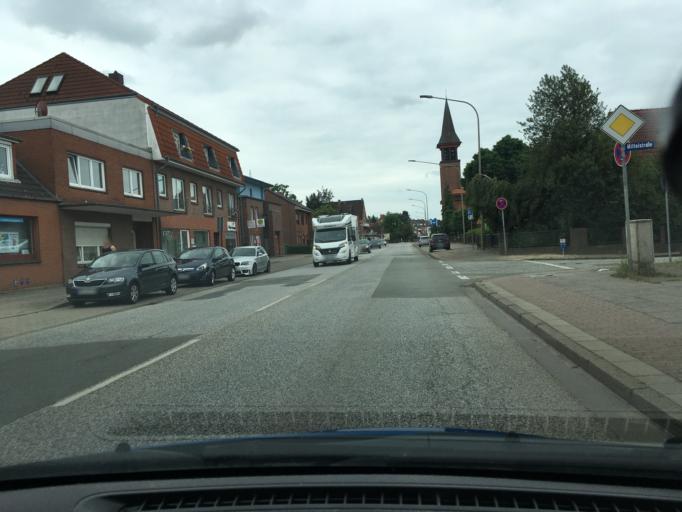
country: DE
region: Schleswig-Holstein
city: Geesthacht
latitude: 53.4419
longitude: 10.3645
